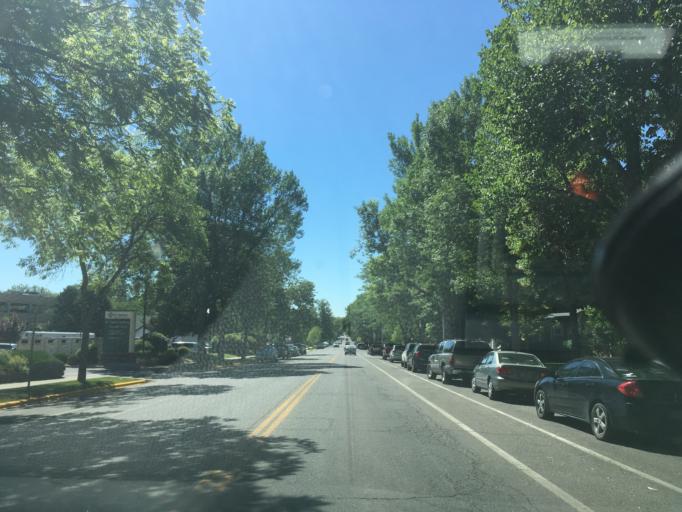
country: US
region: Montana
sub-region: Yellowstone County
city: Billings
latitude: 45.7920
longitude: -108.5192
